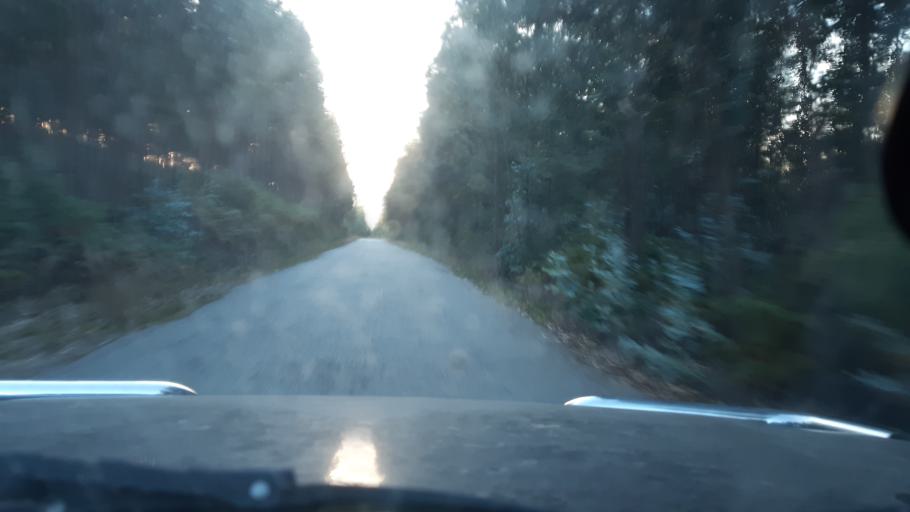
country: PT
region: Aveiro
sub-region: Agueda
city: Aguada de Cima
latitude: 40.5636
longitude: -8.3408
